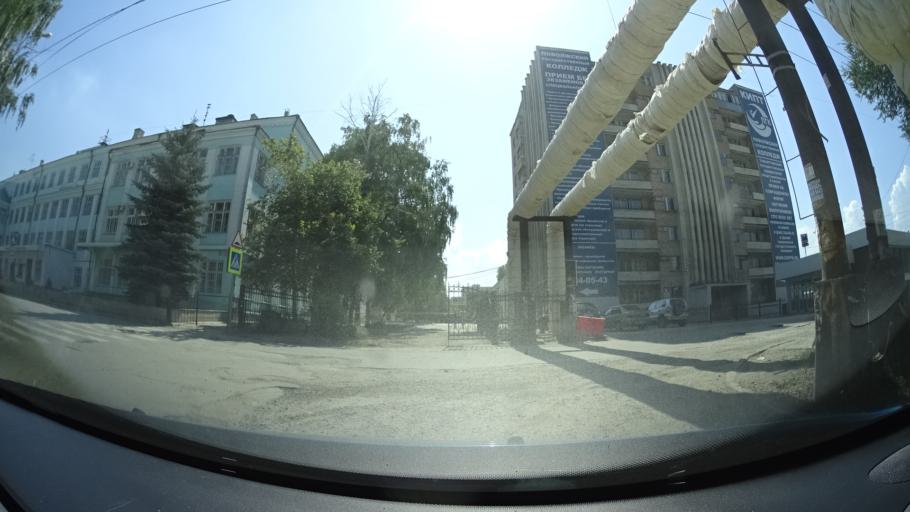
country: RU
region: Samara
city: Samara
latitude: 53.2125
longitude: 50.1494
